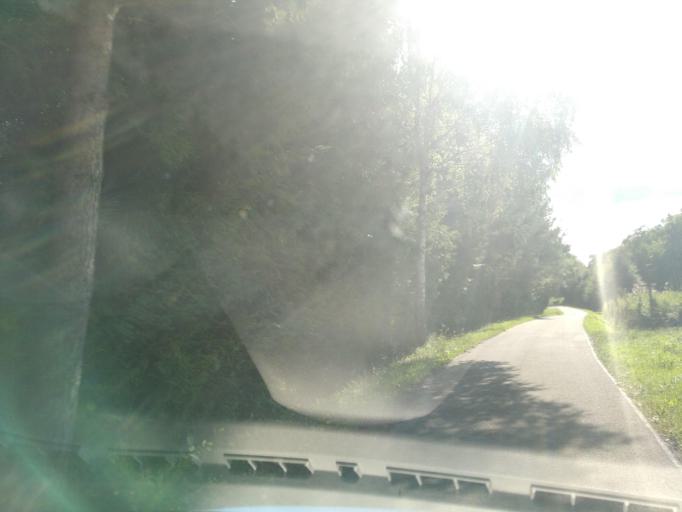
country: PL
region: Subcarpathian Voivodeship
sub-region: Powiat strzyzowski
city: Polomia
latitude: 49.8991
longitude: 21.9176
